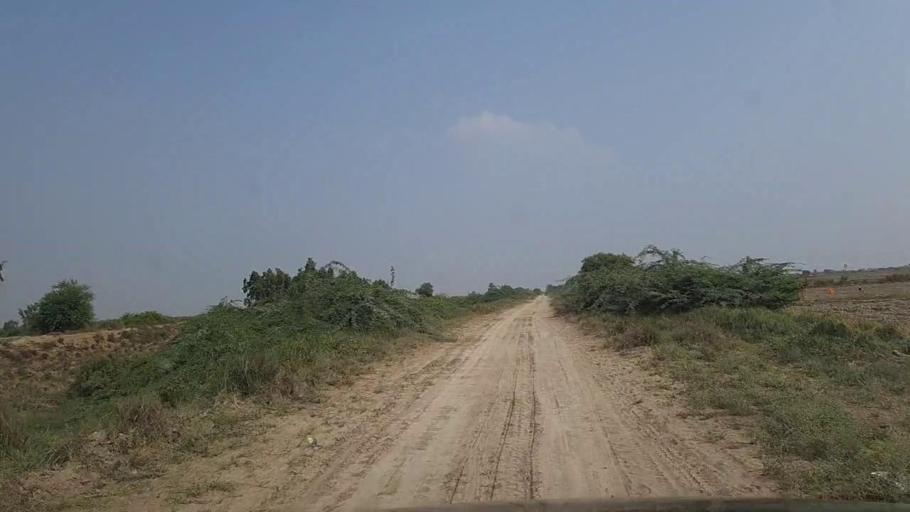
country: PK
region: Sindh
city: Thatta
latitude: 24.7635
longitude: 67.8146
